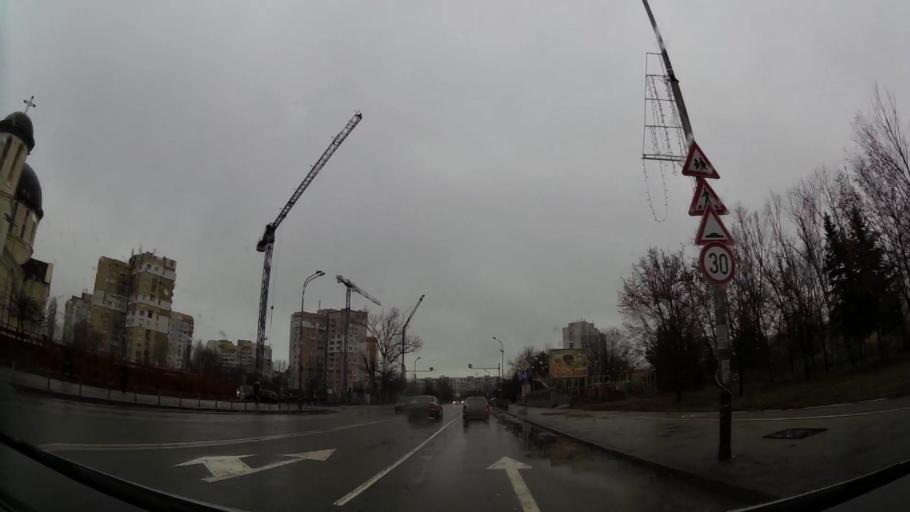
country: BG
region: Sofia-Capital
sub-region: Stolichna Obshtina
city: Sofia
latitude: 42.6433
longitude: 23.3798
